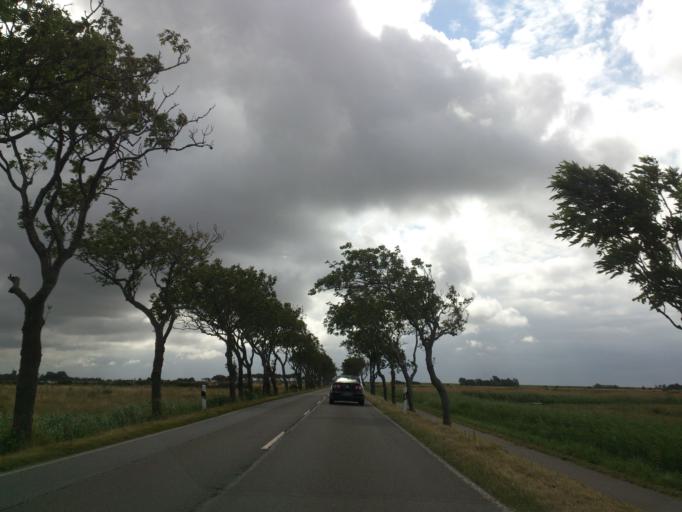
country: DE
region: Schleswig-Holstein
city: Sankt Peter-Ording
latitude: 54.3014
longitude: 8.6768
